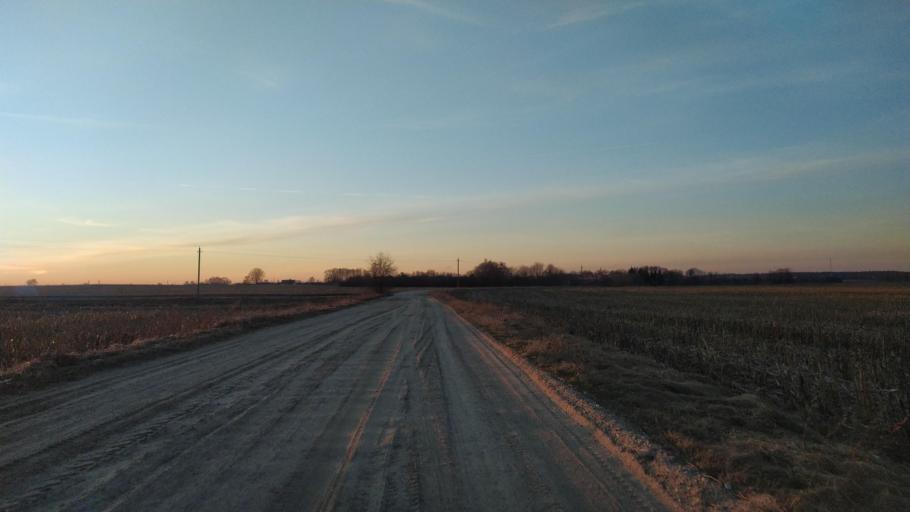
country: BY
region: Brest
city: Pruzhany
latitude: 52.5481
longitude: 24.2369
